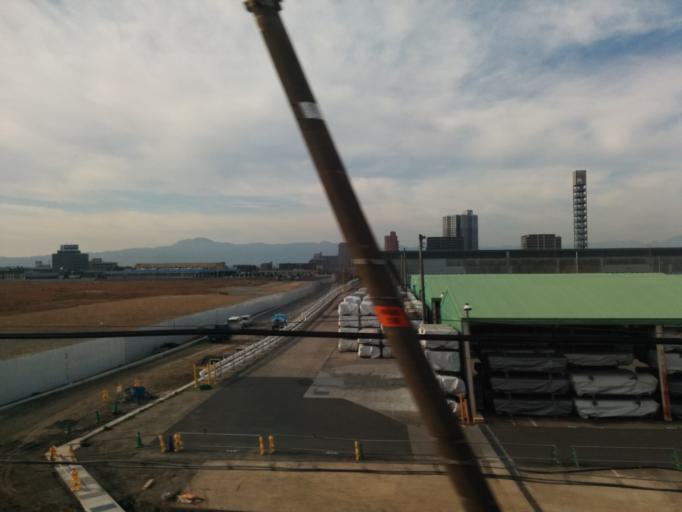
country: JP
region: Shiga Prefecture
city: Kusatsu
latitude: 35.0312
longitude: 135.9916
